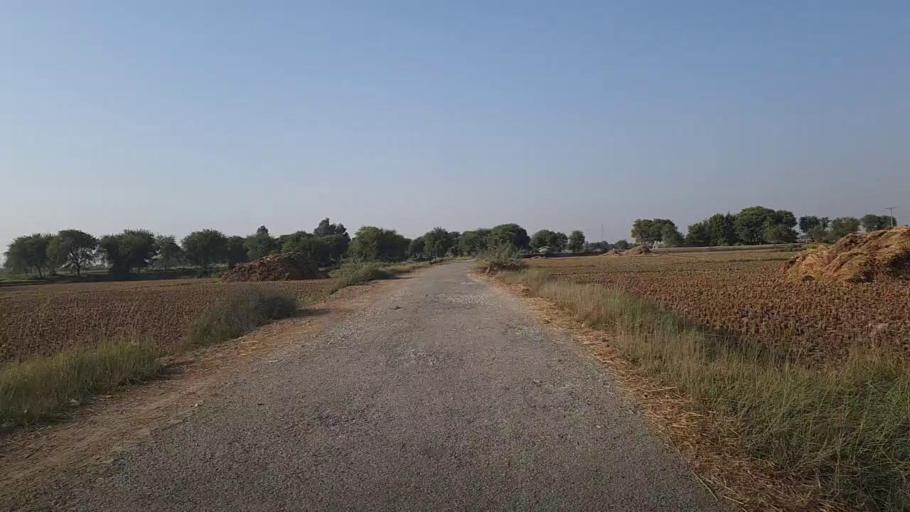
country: PK
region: Sindh
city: Kashmor
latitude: 28.4210
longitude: 69.4084
